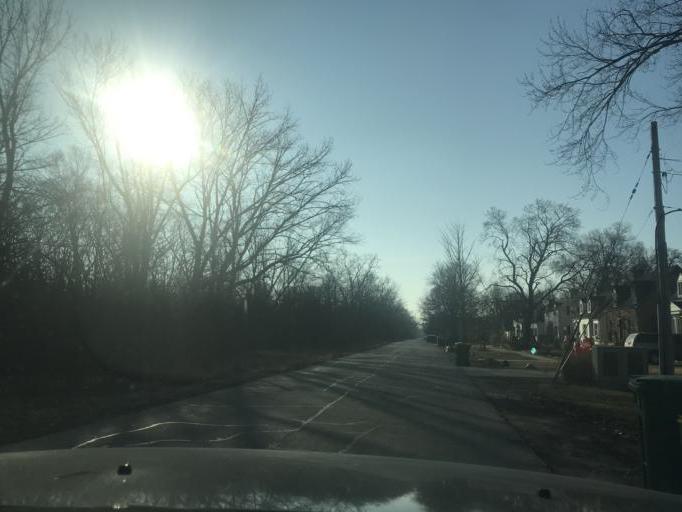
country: US
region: Illinois
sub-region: Cook County
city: Northfield
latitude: 42.1011
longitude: -87.7613
